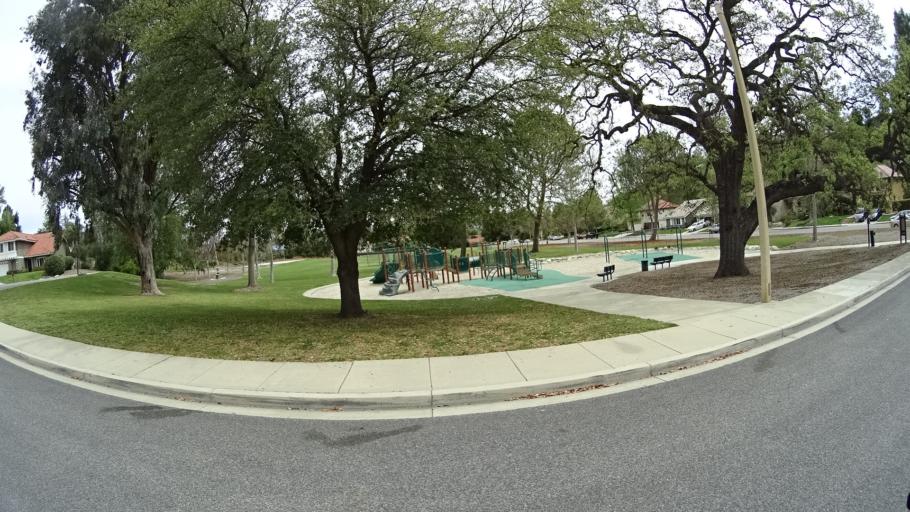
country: US
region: California
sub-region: Ventura County
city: Thousand Oaks
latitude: 34.1433
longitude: -118.8417
